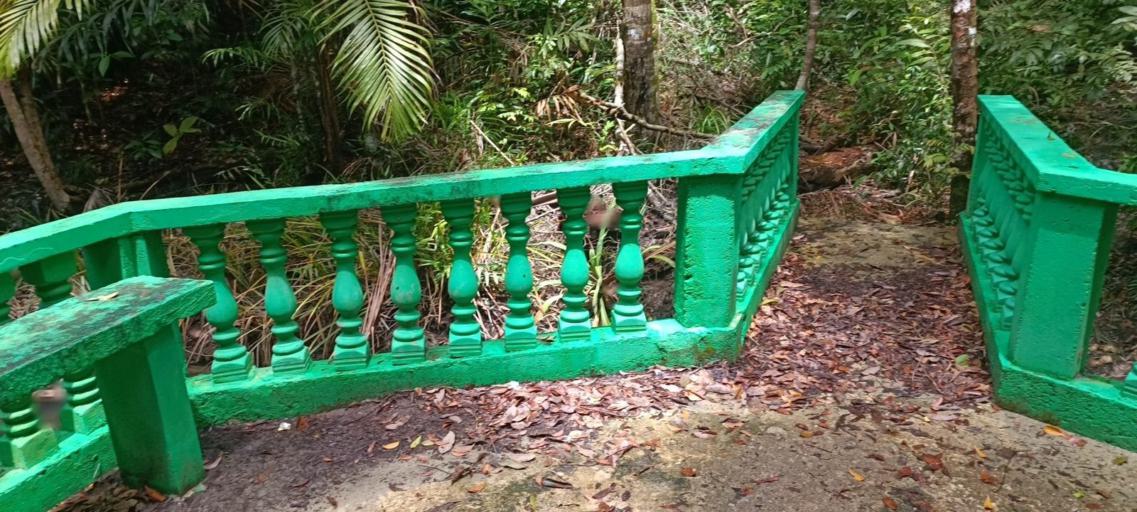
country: MY
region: Penang
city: Tanjung Tokong
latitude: 5.4524
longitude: 100.1878
